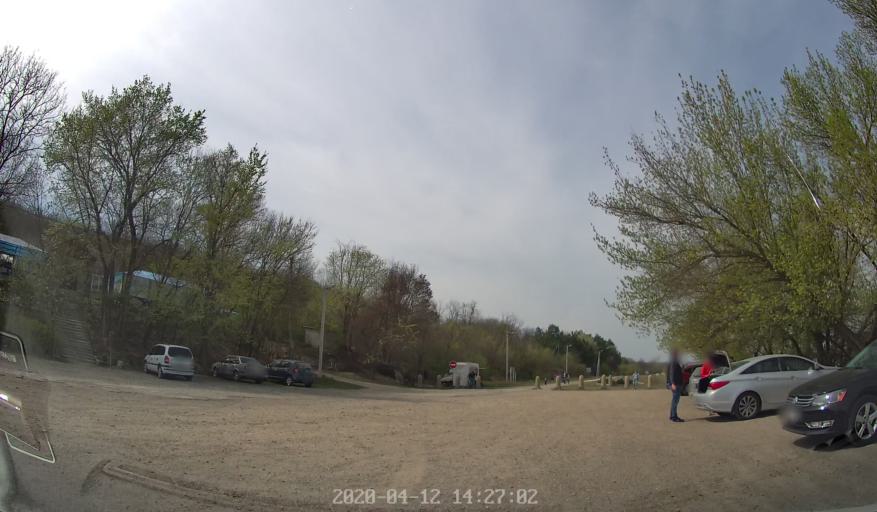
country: MD
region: Telenesti
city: Cocieri
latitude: 47.2760
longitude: 29.1176
